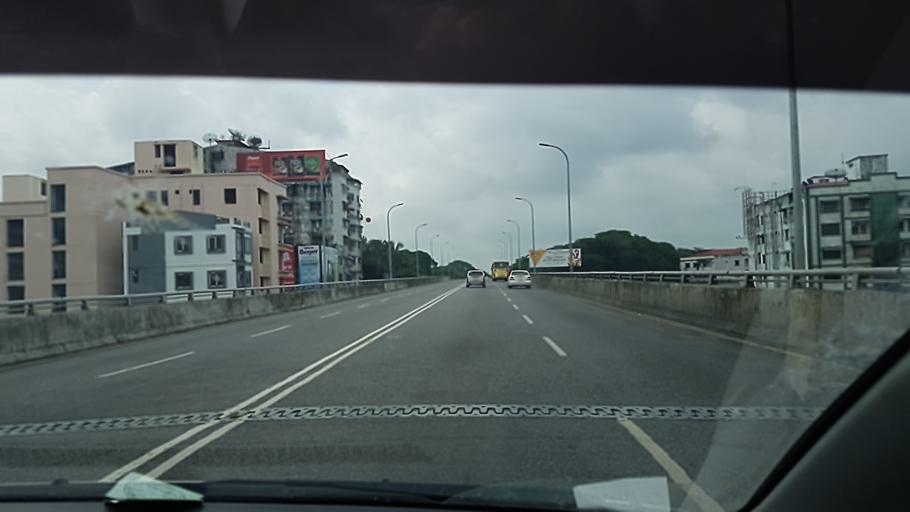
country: MM
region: Yangon
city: Yangon
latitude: 16.8033
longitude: 96.1375
